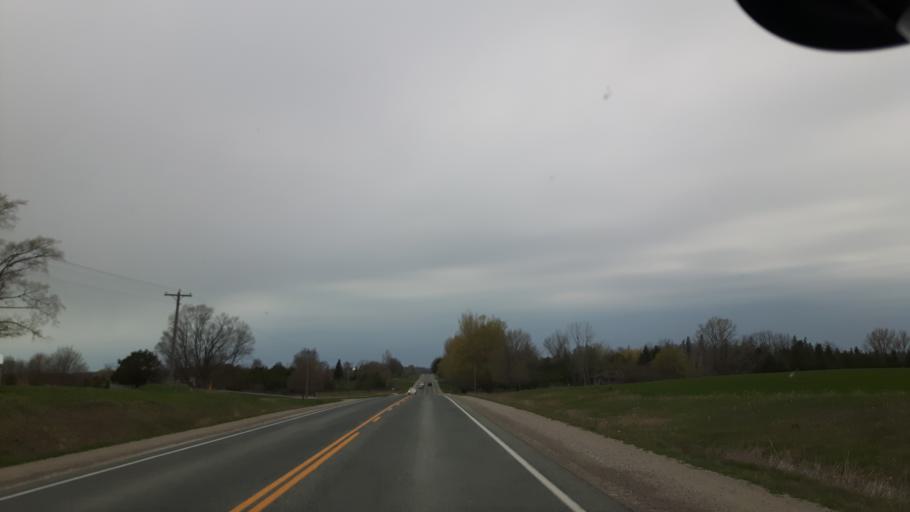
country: CA
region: Ontario
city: Bluewater
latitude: 43.6298
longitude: -81.5691
